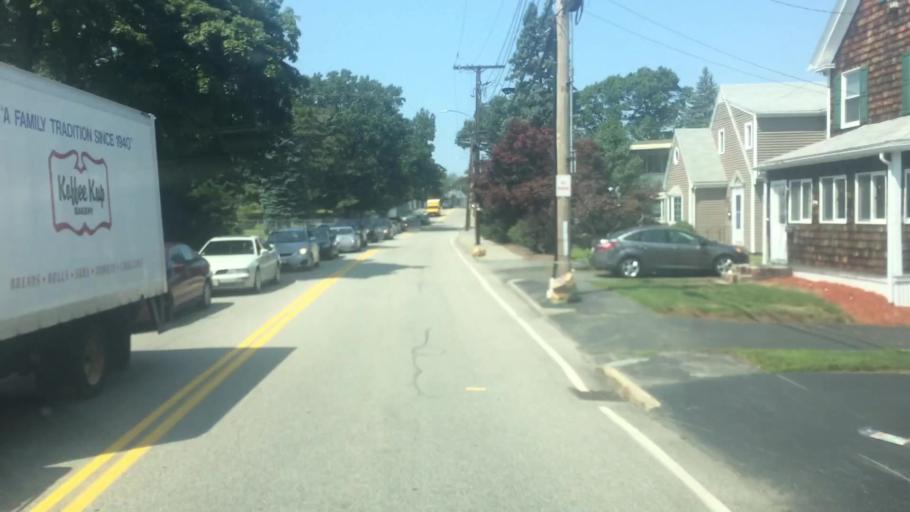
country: US
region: Massachusetts
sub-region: Middlesex County
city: Woburn
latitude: 42.4876
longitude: -71.1418
